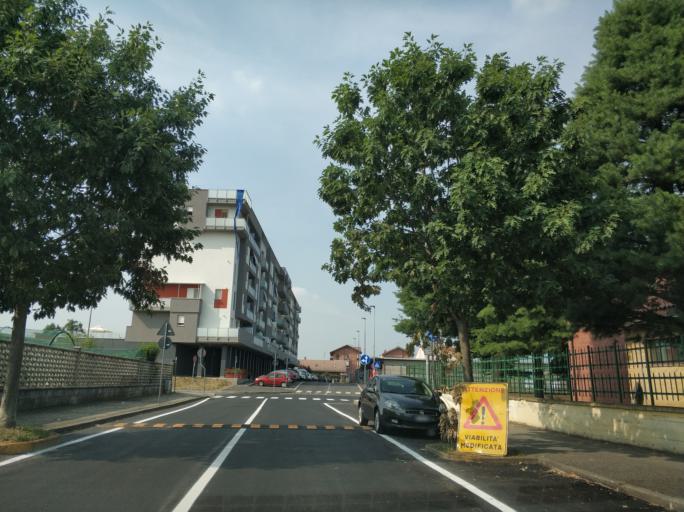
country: IT
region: Piedmont
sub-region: Provincia di Torino
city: Leini
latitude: 45.1506
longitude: 7.7041
